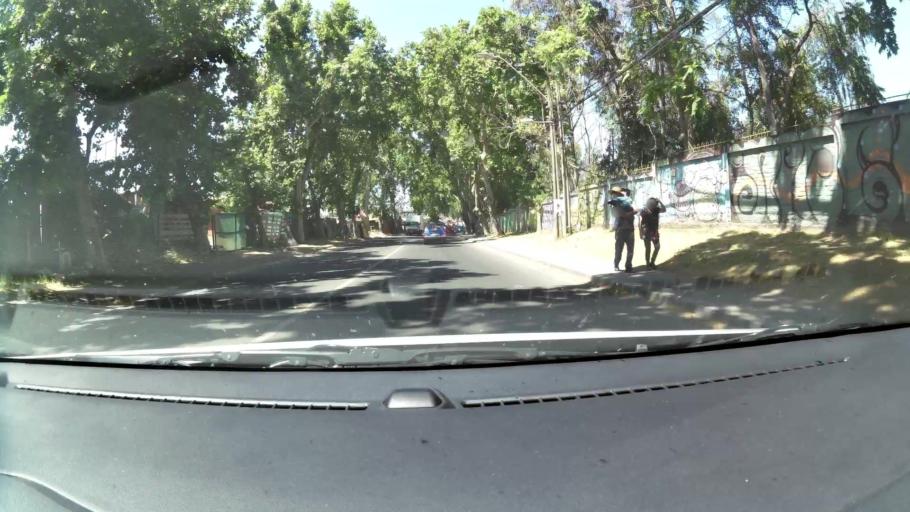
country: CL
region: Santiago Metropolitan
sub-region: Provincia de Maipo
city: San Bernardo
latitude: -33.6212
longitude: -70.7003
